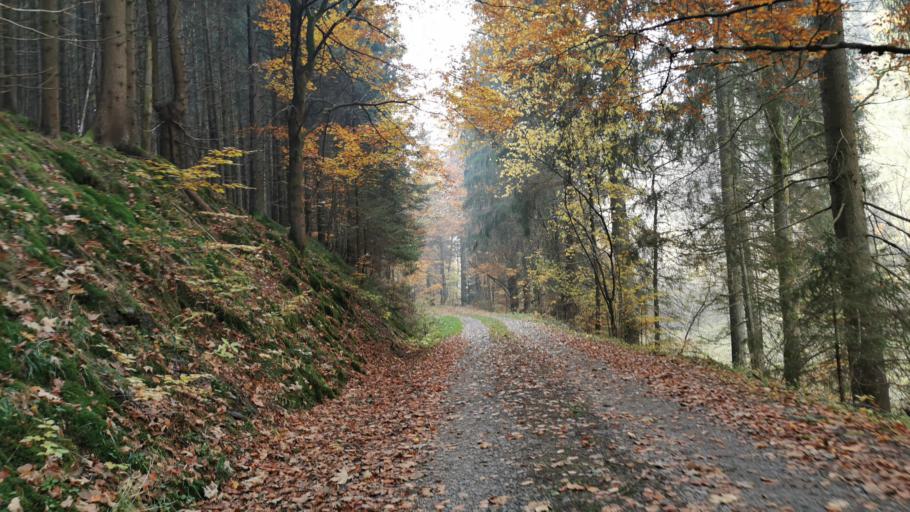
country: DE
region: Bavaria
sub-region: Upper Franconia
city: Nordhalben
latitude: 50.3899
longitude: 11.5305
